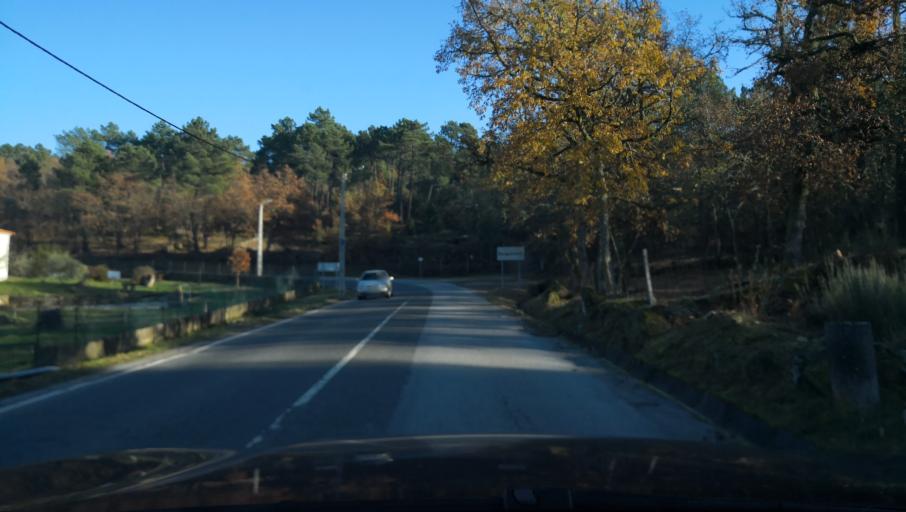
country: PT
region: Vila Real
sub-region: Vila Real
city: Vila Real
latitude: 41.3294
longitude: -7.6695
